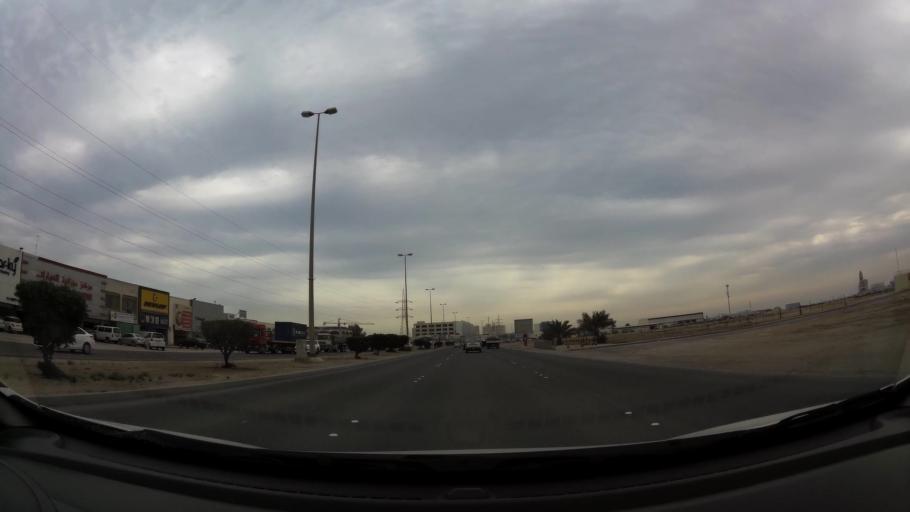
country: BH
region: Northern
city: Sitrah
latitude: 26.1538
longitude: 50.6135
